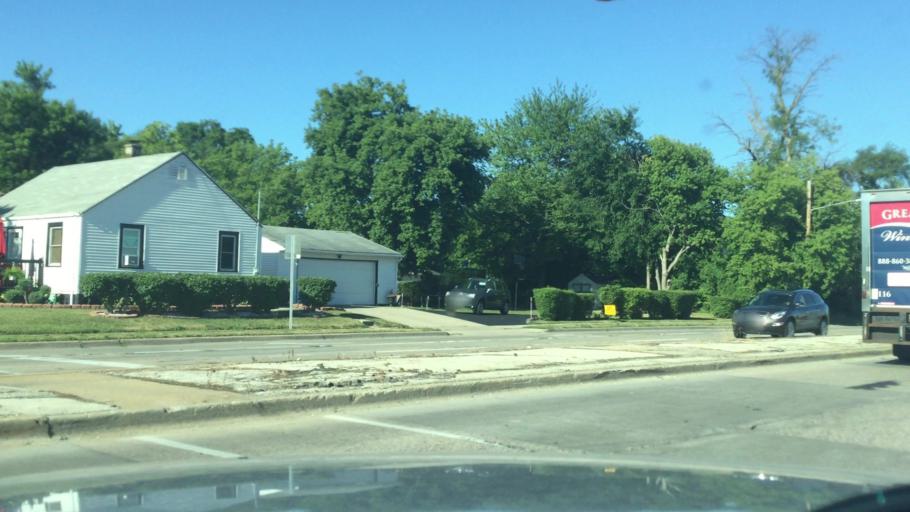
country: US
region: Michigan
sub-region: Saginaw County
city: Saginaw
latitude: 43.4103
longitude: -83.9361
